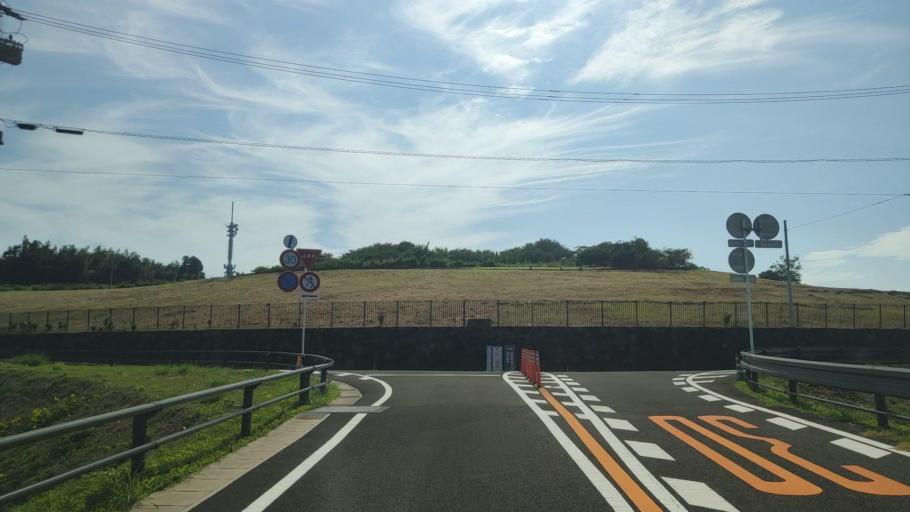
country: JP
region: Shizuoka
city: Shizuoka-shi
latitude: 34.9794
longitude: 138.4692
